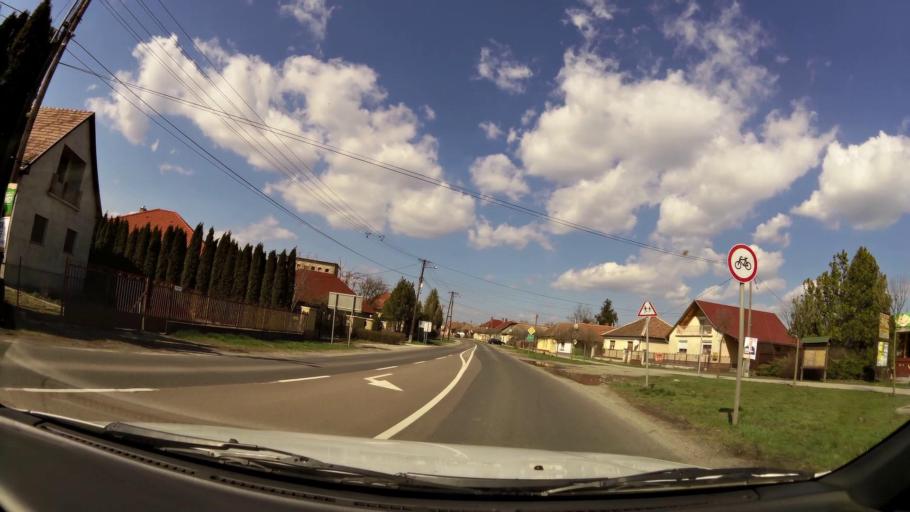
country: HU
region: Pest
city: Tapioszele
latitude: 47.3246
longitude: 19.8772
